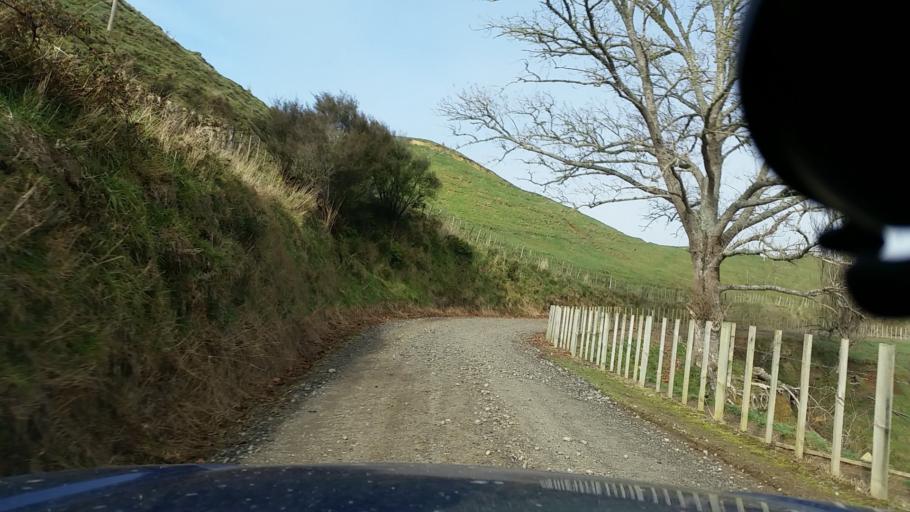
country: NZ
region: Taranaki
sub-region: New Plymouth District
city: Waitara
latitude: -38.9971
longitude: 174.7720
